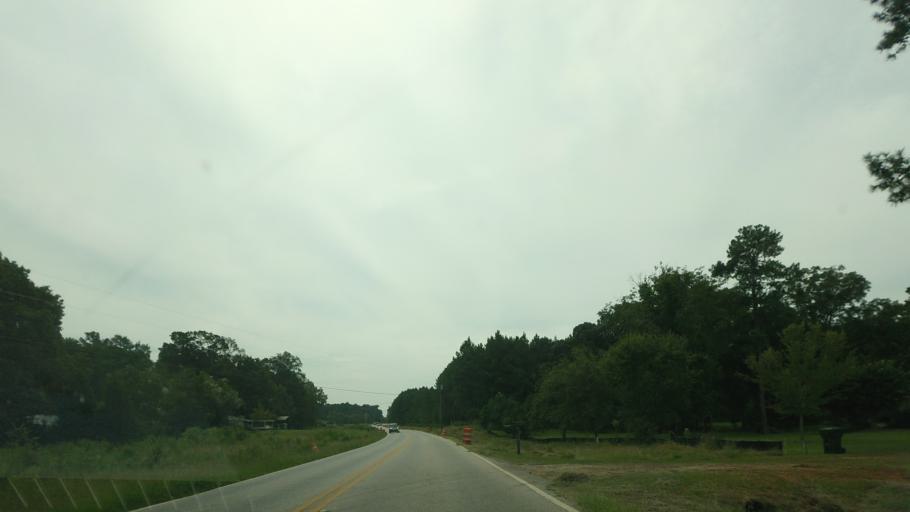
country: US
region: Georgia
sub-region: Houston County
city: Robins Air Force Base
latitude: 32.5474
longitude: -83.5766
